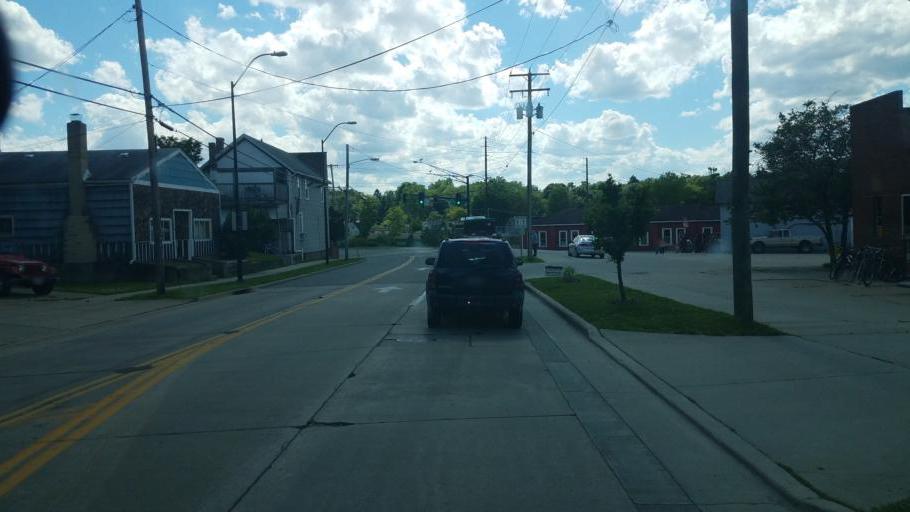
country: US
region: Ohio
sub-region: Portage County
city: Kent
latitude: 41.1591
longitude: -81.3571
